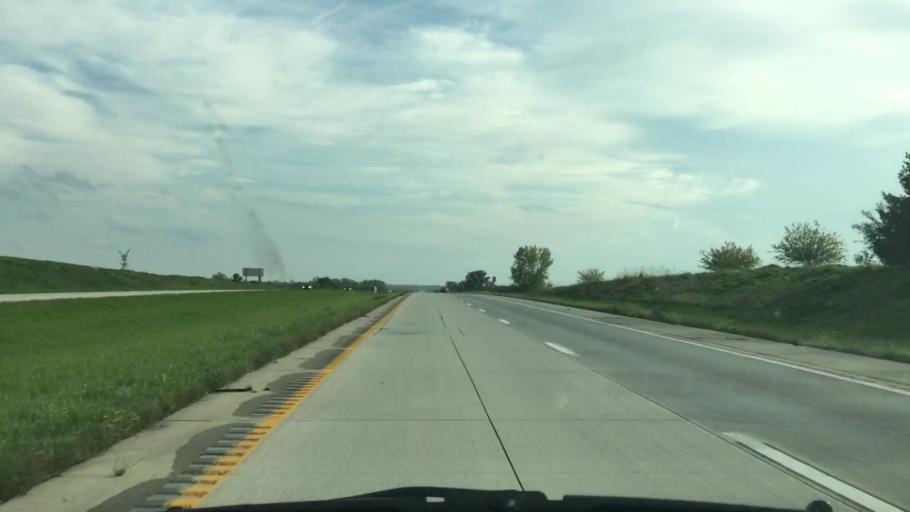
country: US
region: Missouri
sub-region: Daviess County
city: Gallatin
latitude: 40.0717
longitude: -94.0938
